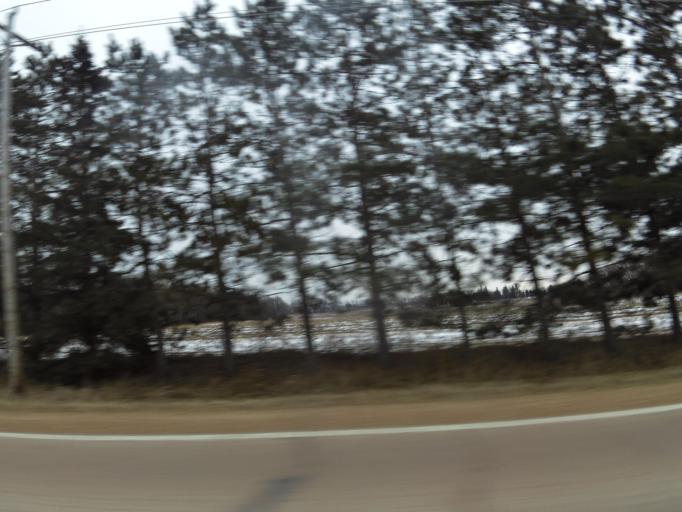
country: US
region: Minnesota
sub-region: Carver County
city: Carver
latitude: 44.7312
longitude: -93.6843
